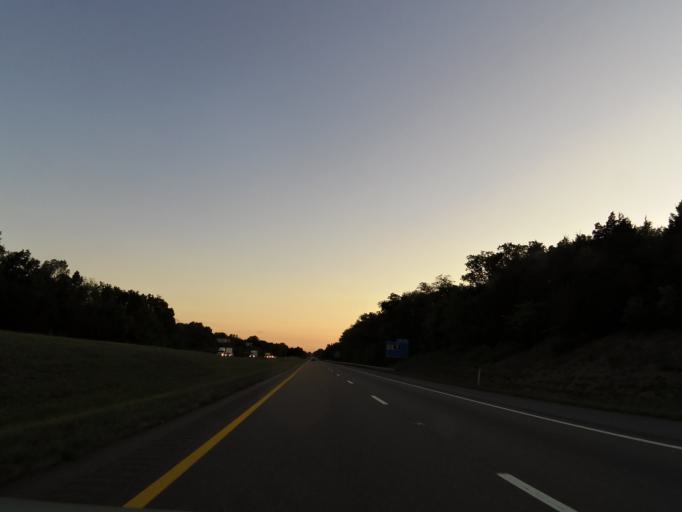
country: US
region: Tennessee
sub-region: Hamblen County
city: Morristown
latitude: 36.1803
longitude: -83.1993
